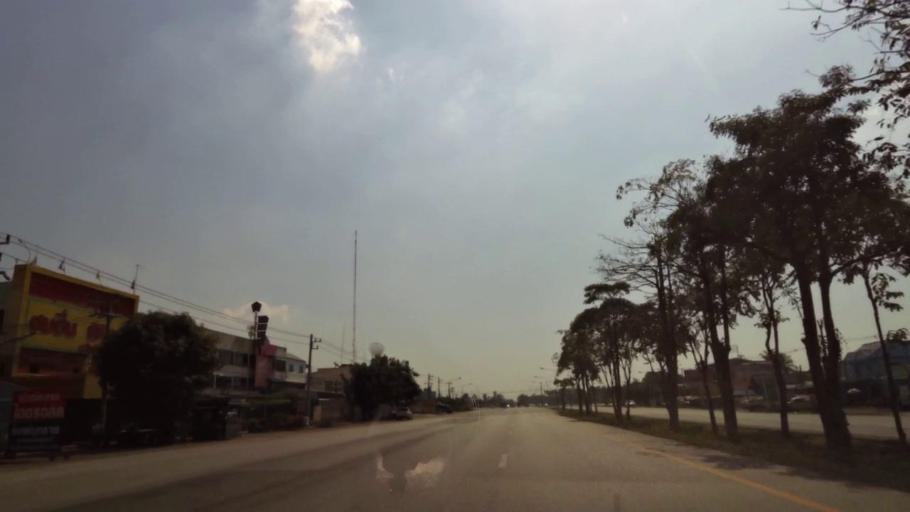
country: TH
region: Phichit
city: Bueng Na Rang
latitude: 16.1267
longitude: 100.1256
